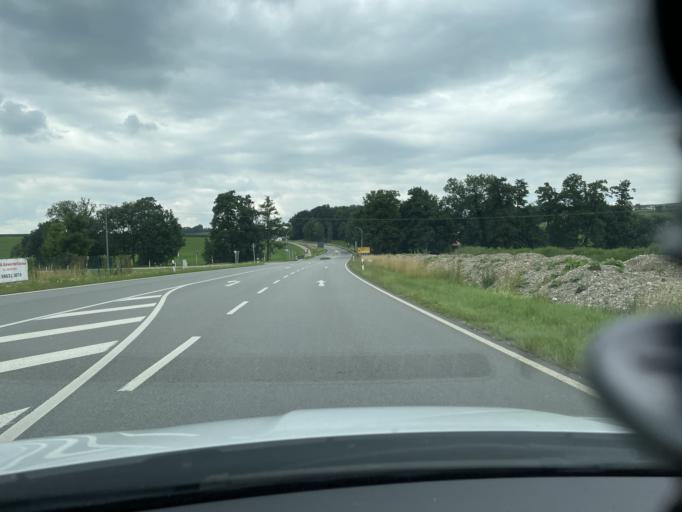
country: DE
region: Bavaria
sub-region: Upper Bavaria
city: Haag in Oberbayern
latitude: 48.1693
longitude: 12.1623
